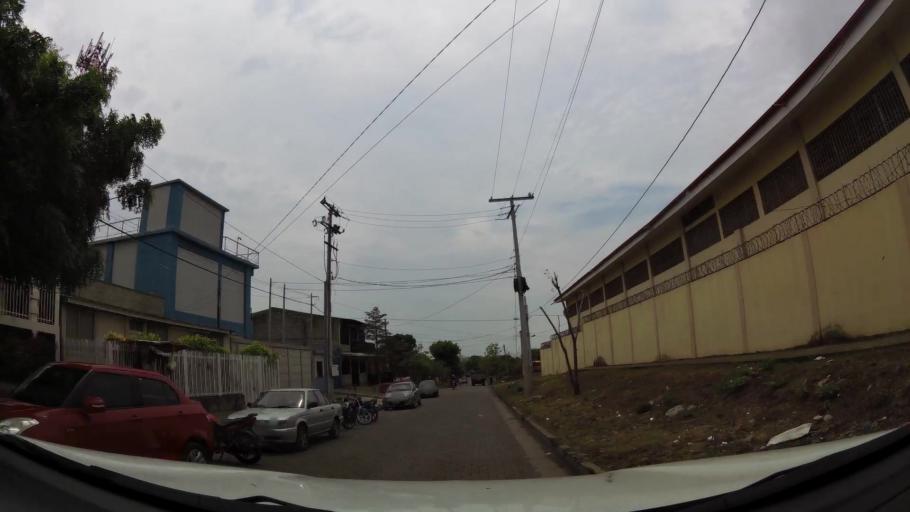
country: NI
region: Granada
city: Granada
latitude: 11.9331
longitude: -85.9645
